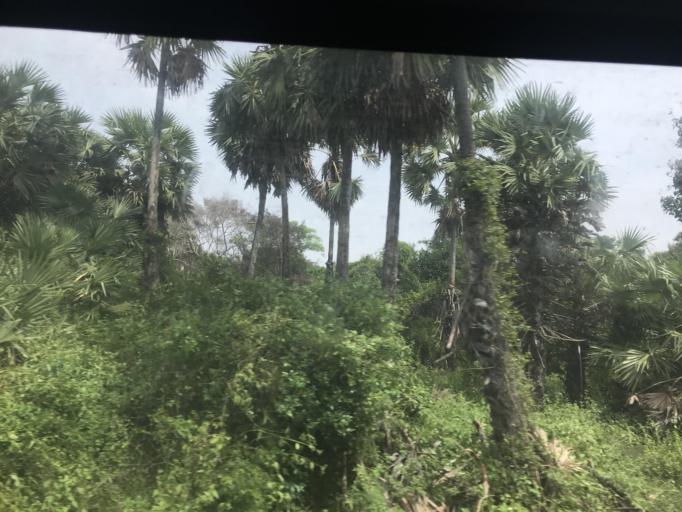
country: LK
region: Northern Province
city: Kilinochchi
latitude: 9.5677
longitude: 80.3630
